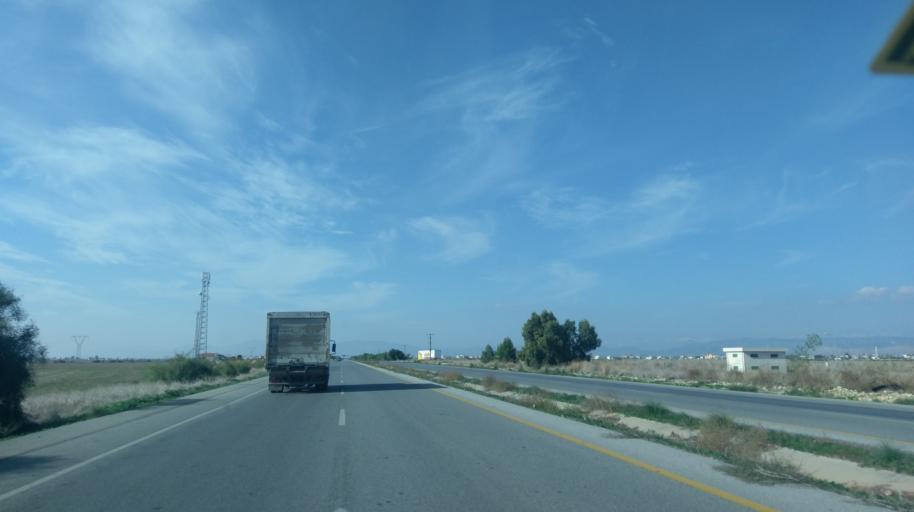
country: CY
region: Ammochostos
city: Acheritou
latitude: 35.1566
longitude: 33.8403
